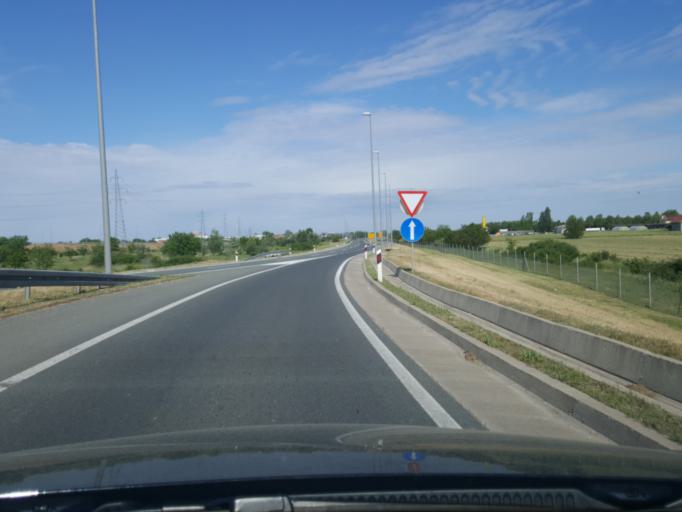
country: RS
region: Autonomna Pokrajina Vojvodina
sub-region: Juznobacki Okrug
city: Novi Sad
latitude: 45.3053
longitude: 19.8100
